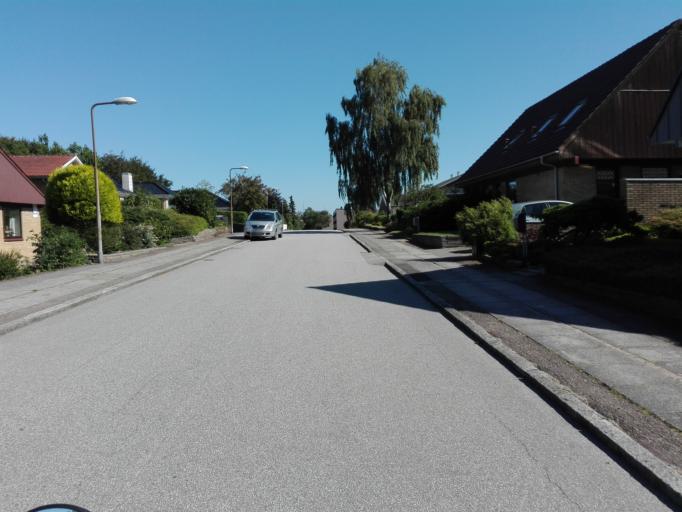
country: DK
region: Central Jutland
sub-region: Arhus Kommune
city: Stavtrup
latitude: 56.1108
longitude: 10.1465
